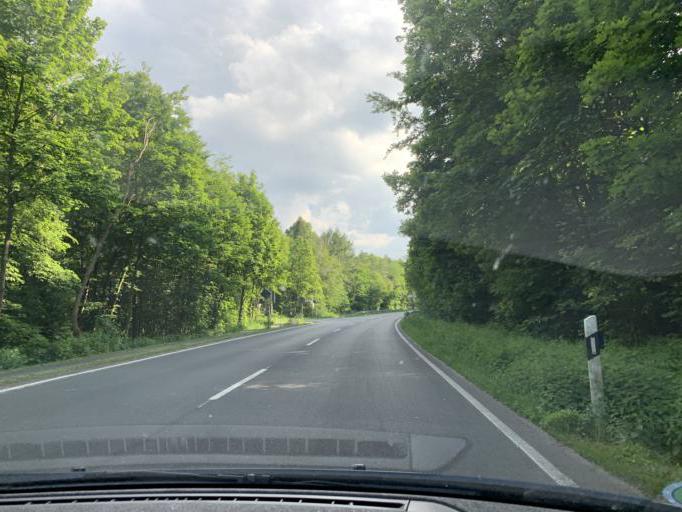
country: DE
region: North Rhine-Westphalia
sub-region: Regierungsbezirk Koln
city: Weilerswist
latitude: 50.7936
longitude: 6.8685
